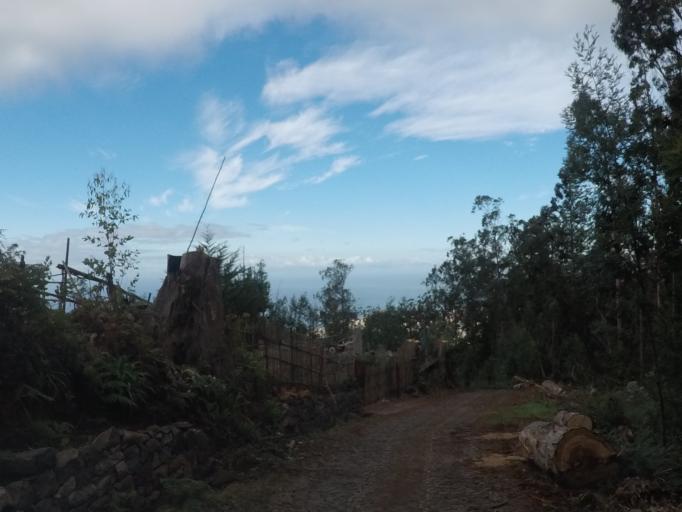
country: PT
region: Madeira
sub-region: Funchal
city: Nossa Senhora do Monte
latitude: 32.6745
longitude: -16.8806
